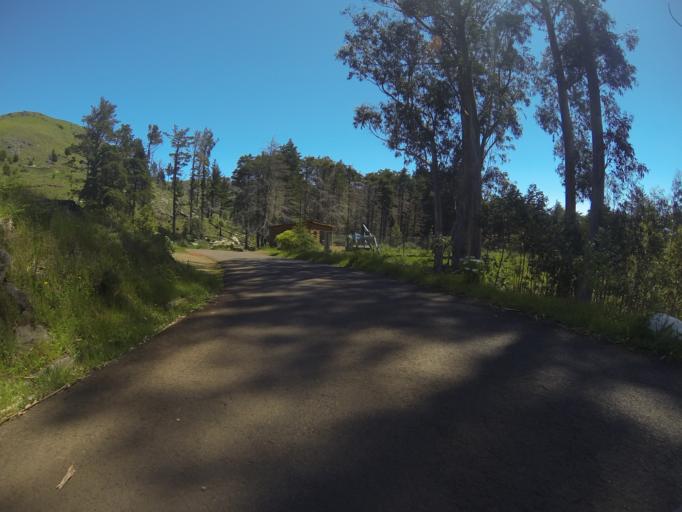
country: PT
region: Madeira
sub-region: Funchal
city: Nossa Senhora do Monte
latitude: 32.6998
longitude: -16.9060
